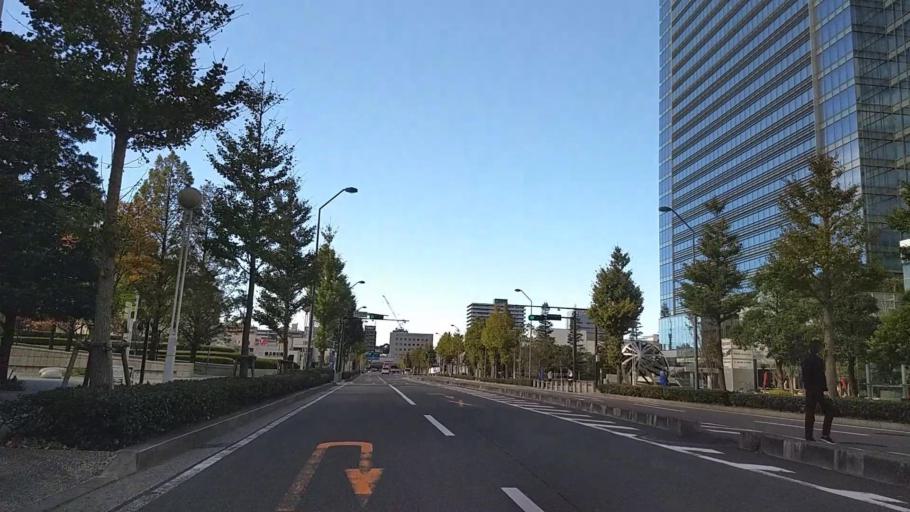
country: JP
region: Kanagawa
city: Yokohama
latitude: 35.4584
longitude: 139.6307
